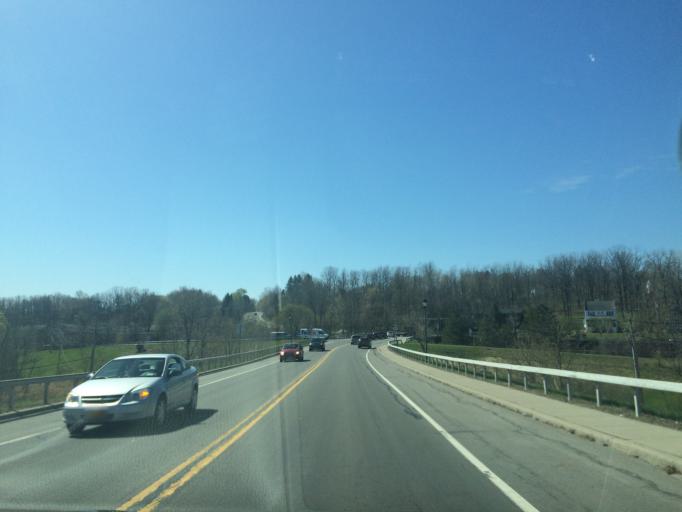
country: US
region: New York
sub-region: Monroe County
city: Fairport
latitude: 43.0989
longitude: -77.4324
